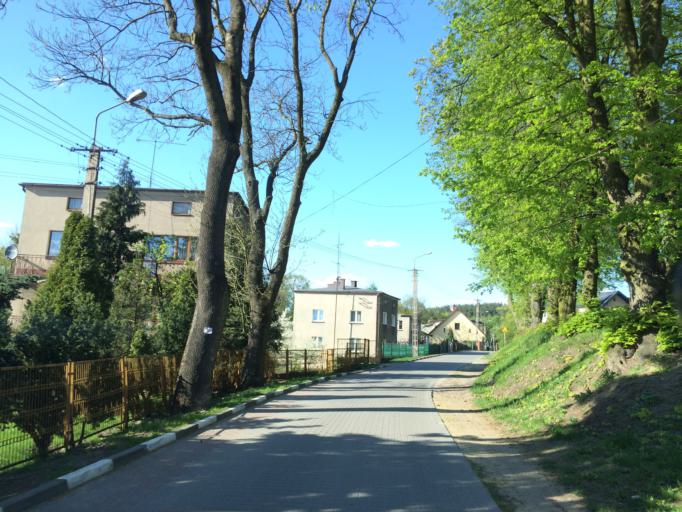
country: PL
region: Warmian-Masurian Voivodeship
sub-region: Powiat dzialdowski
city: Lidzbark
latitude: 53.2652
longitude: 19.8178
